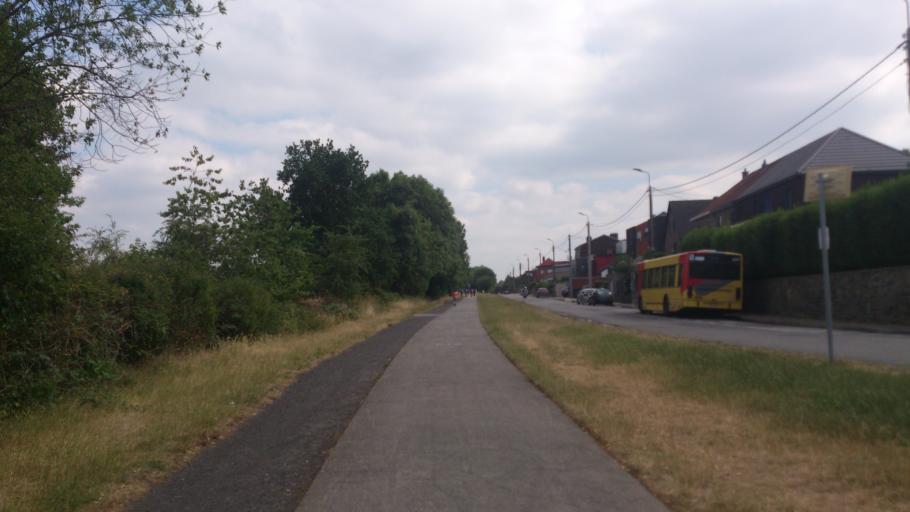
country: BE
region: Wallonia
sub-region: Province de Liege
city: Herstal
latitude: 50.6329
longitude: 5.6324
